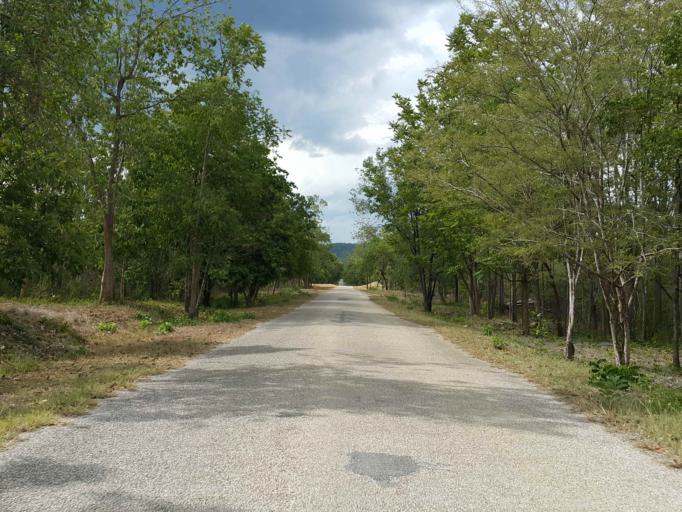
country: TH
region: Sukhothai
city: Thung Saliam
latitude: 17.3362
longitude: 99.4239
